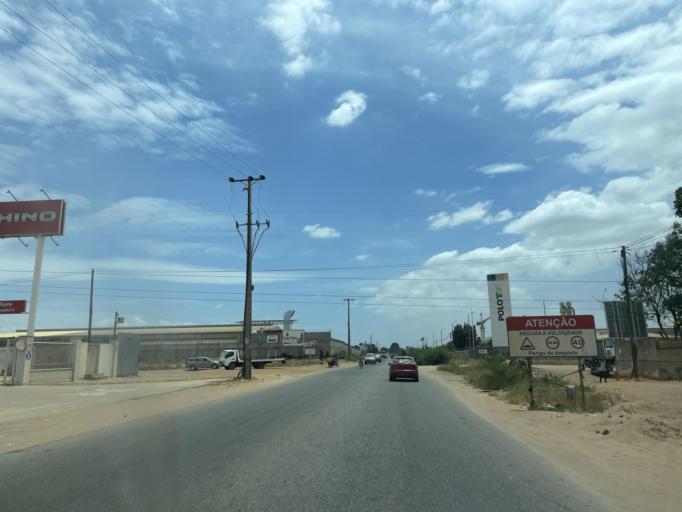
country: AO
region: Luanda
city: Luanda
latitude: -8.9279
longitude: 13.3959
